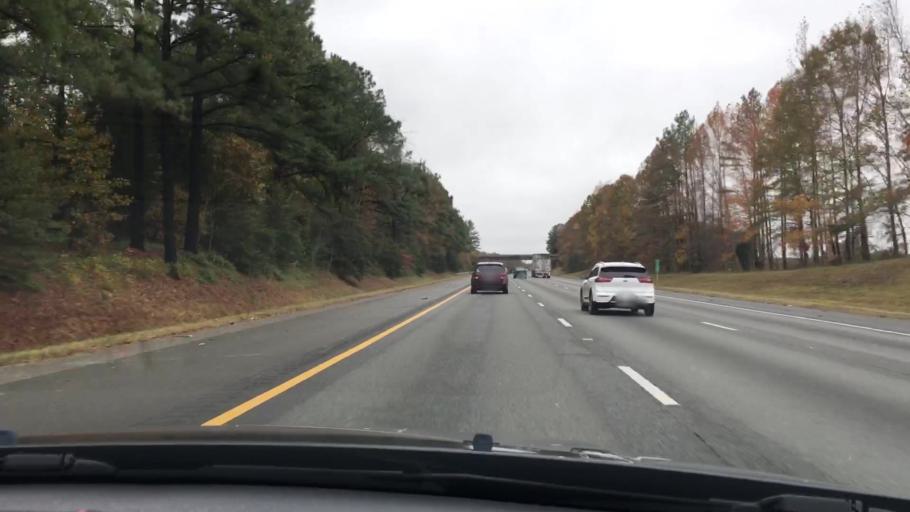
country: US
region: Virginia
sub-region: Caroline County
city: Bowling Green
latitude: 37.9971
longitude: -77.4946
